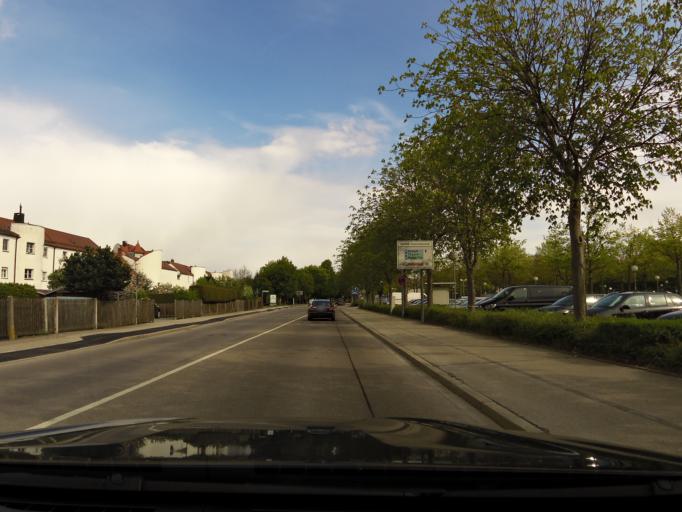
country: DE
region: Bavaria
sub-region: Upper Bavaria
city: Ingolstadt
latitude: 48.7613
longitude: 11.4203
